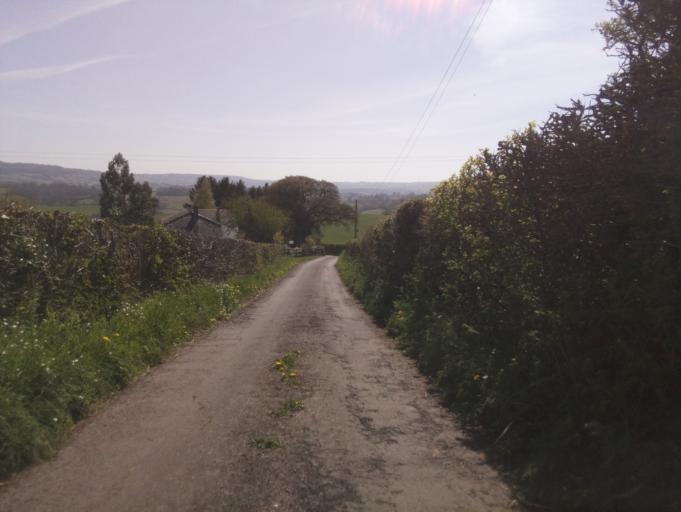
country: GB
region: Wales
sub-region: Monmouthshire
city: Llangwm
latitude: 51.7427
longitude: -2.8272
